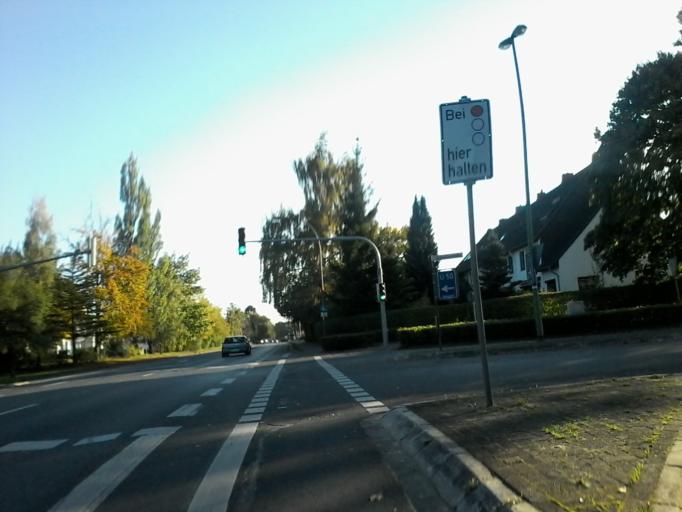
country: DE
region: Lower Saxony
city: Achim
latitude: 53.0207
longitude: 9.0314
